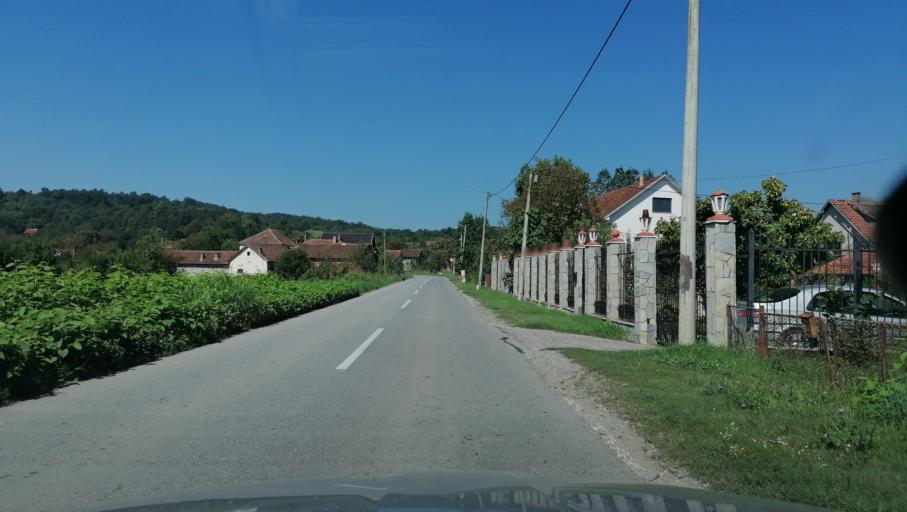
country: RS
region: Central Serbia
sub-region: Raski Okrug
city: Kraljevo
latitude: 43.7248
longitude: 20.8019
